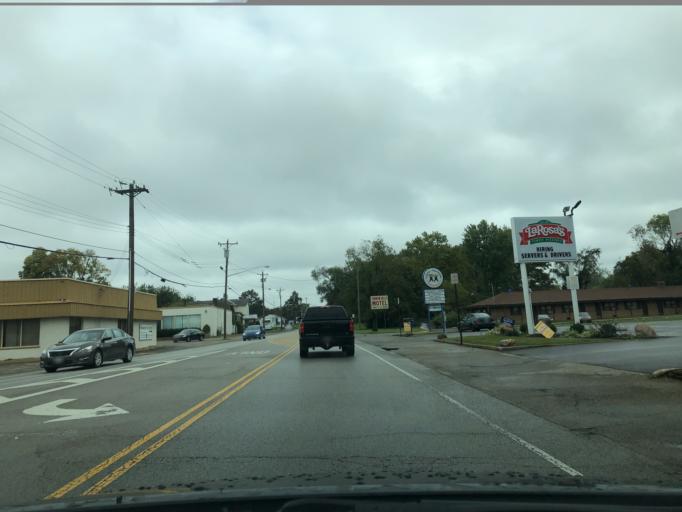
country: US
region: Ohio
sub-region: Hamilton County
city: Sharonville
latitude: 39.2741
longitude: -84.4112
